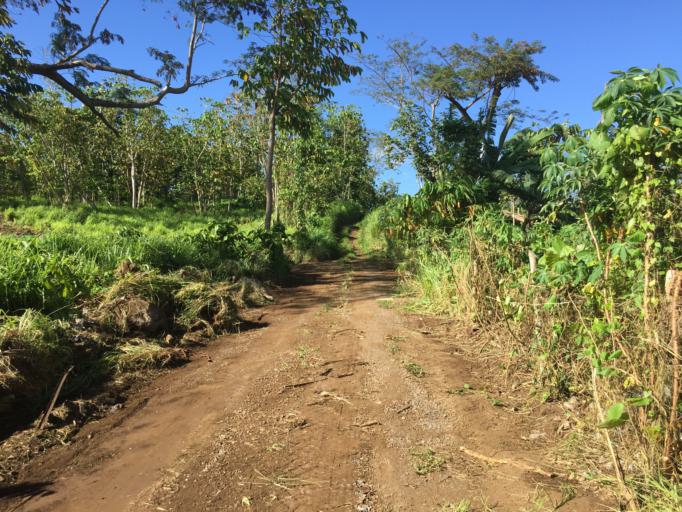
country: WS
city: Siusega
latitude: -13.8344
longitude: -171.8440
